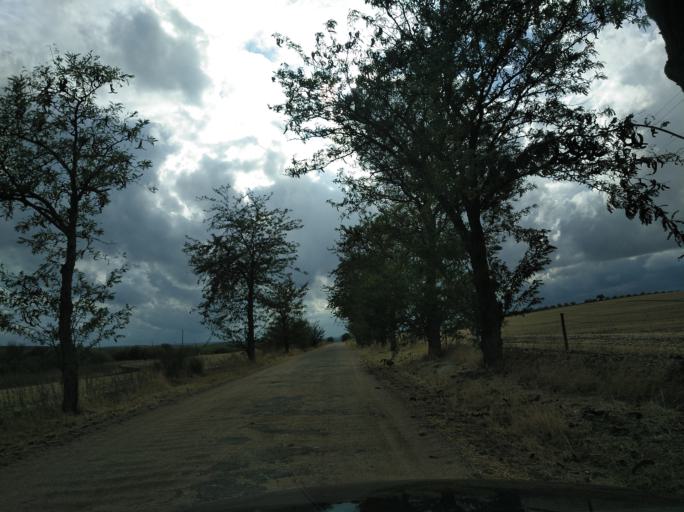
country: PT
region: Portalegre
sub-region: Campo Maior
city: Campo Maior
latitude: 39.0414
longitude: -7.1064
